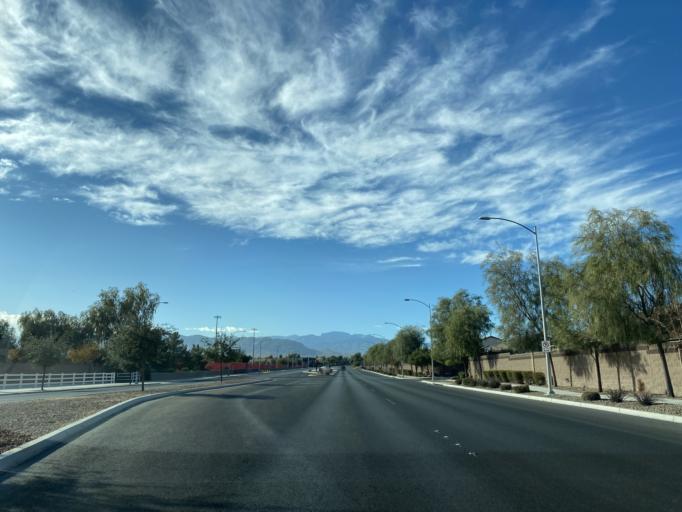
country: US
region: Nevada
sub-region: Clark County
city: North Las Vegas
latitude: 36.3052
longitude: -115.2547
